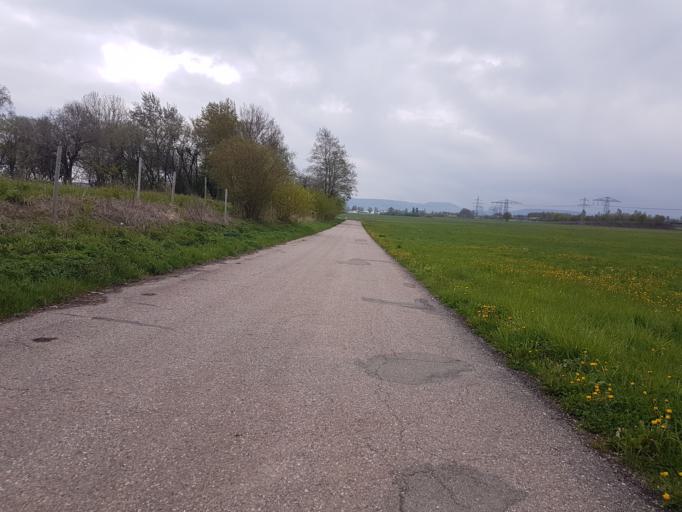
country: DE
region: Baden-Wuerttemberg
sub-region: Freiburg Region
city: Donaueschingen
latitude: 47.9675
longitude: 8.5160
